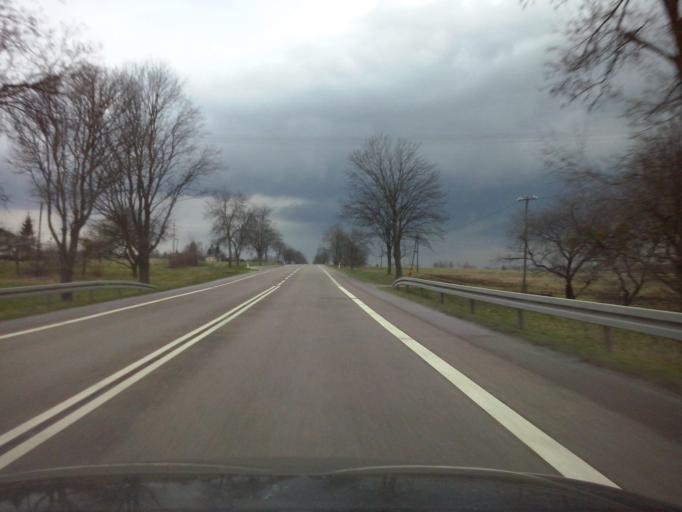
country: PL
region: Lublin Voivodeship
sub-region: Powiat chelmski
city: Rejowiec Fabryczny
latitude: 51.1756
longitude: 23.2489
